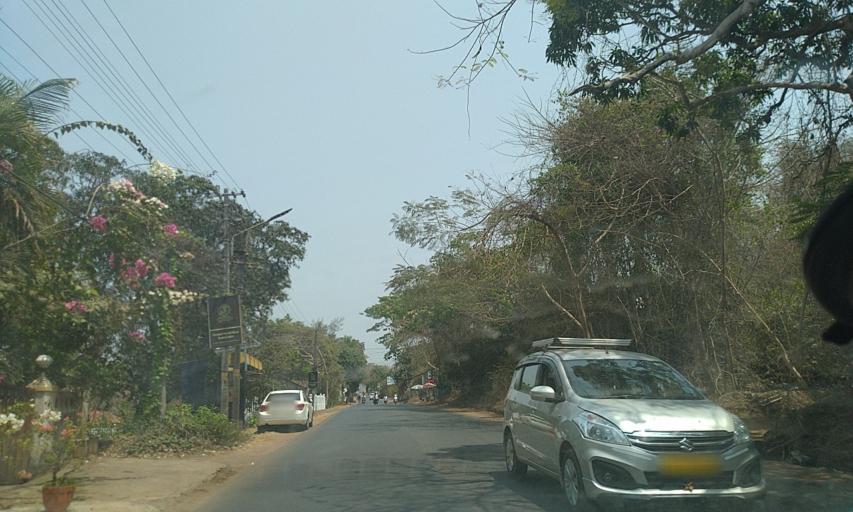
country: IN
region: Goa
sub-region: North Goa
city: Saligao
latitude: 15.5463
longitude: 73.8017
